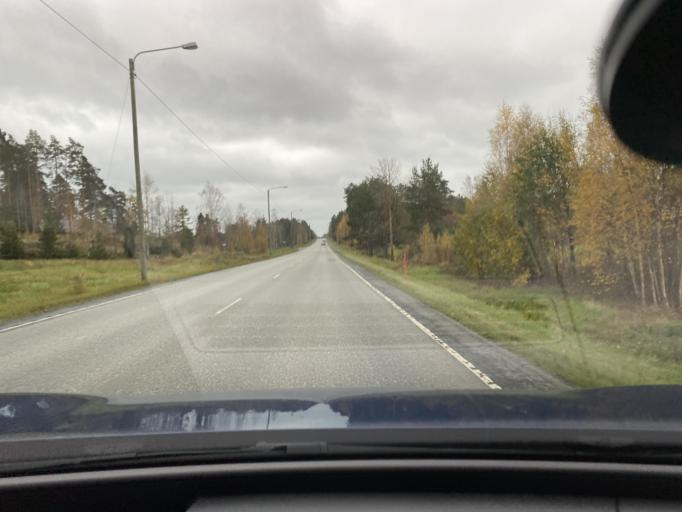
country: FI
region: Varsinais-Suomi
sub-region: Vakka-Suomi
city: Laitila
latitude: 60.9717
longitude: 21.5935
